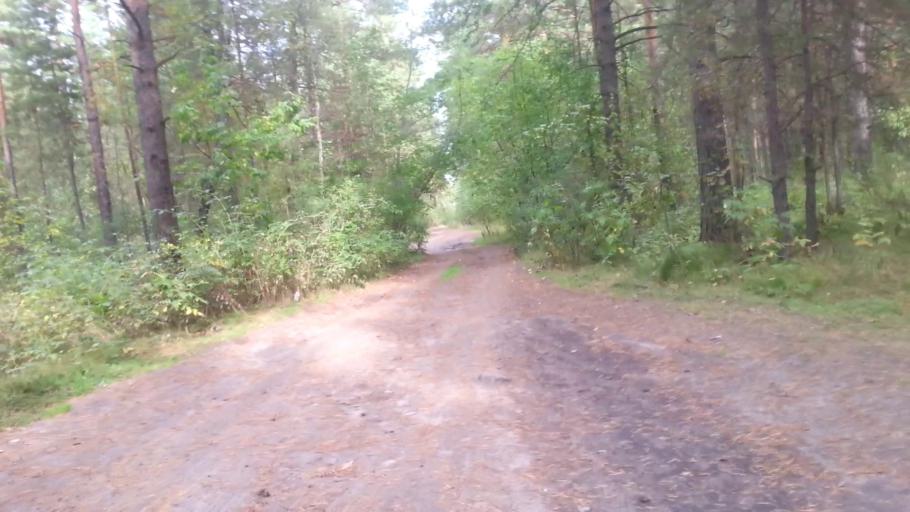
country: RU
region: Altai Krai
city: Yuzhnyy
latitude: 53.3104
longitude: 83.6962
